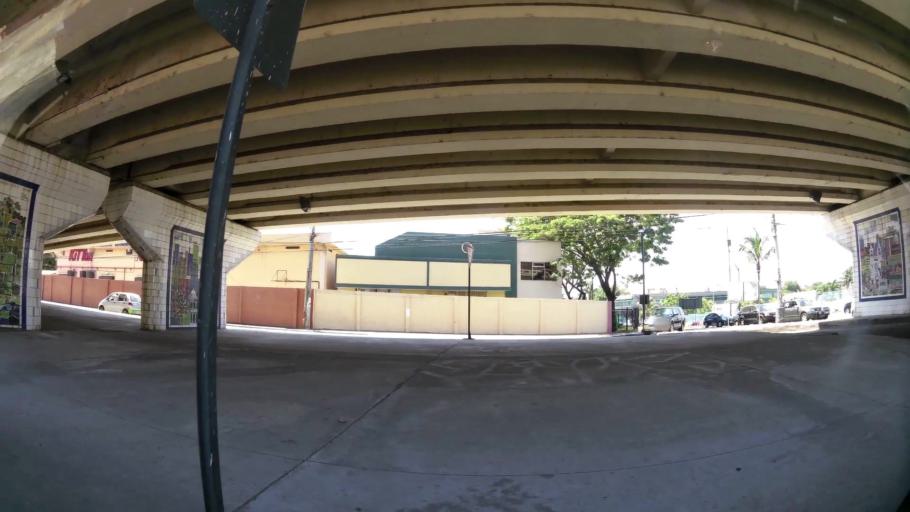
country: EC
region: Guayas
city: Guayaquil
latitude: -2.1738
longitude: -79.9148
